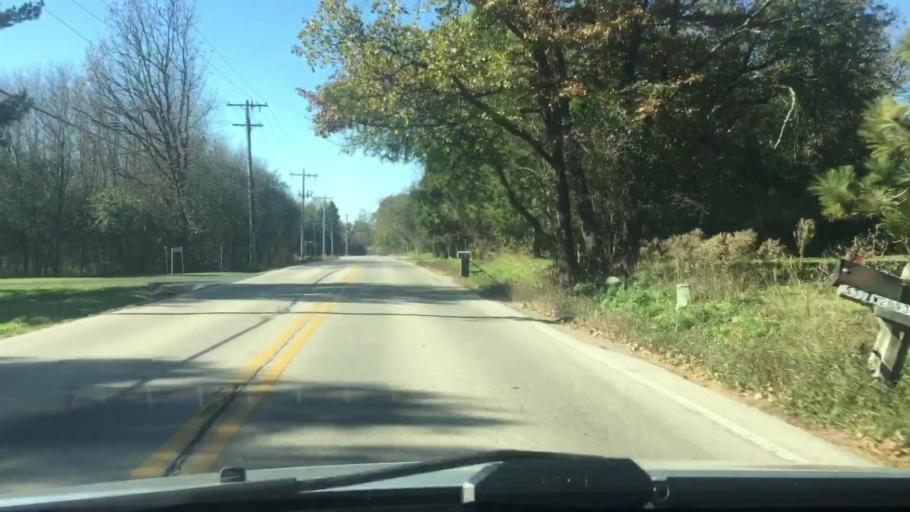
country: US
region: Wisconsin
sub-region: Waukesha County
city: Wales
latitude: 42.9881
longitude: -88.3448
